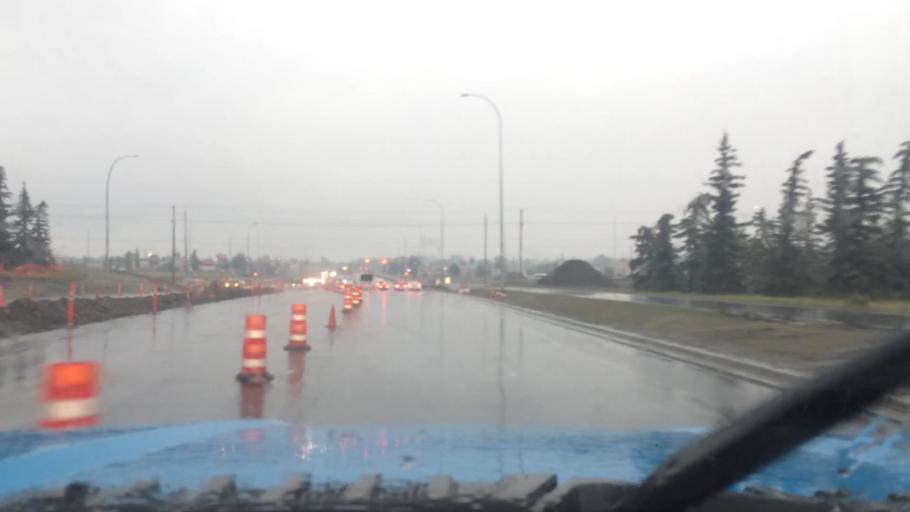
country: CA
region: Alberta
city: Calgary
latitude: 51.0940
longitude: -113.9583
